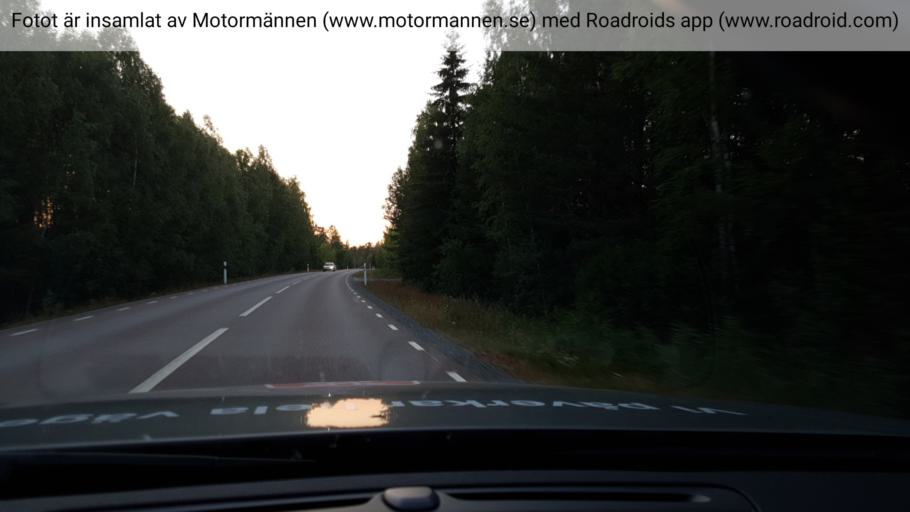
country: SE
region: Uppsala
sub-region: Heby Kommun
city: OEstervala
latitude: 60.0424
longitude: 17.2413
